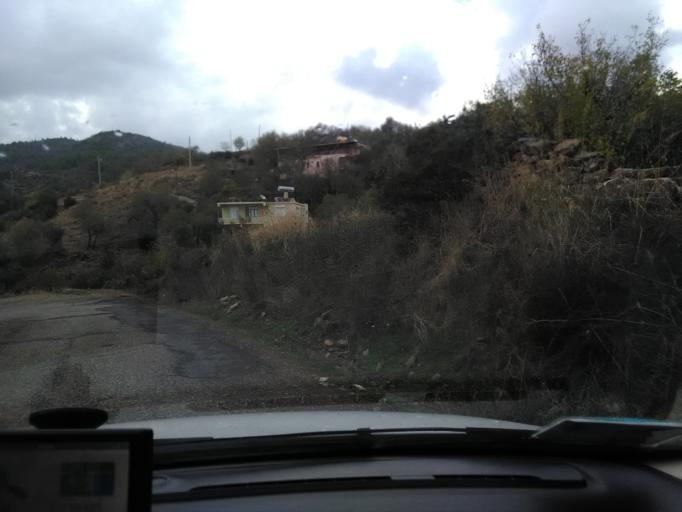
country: TR
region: Antalya
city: Gazipasa
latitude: 36.1552
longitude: 32.4264
